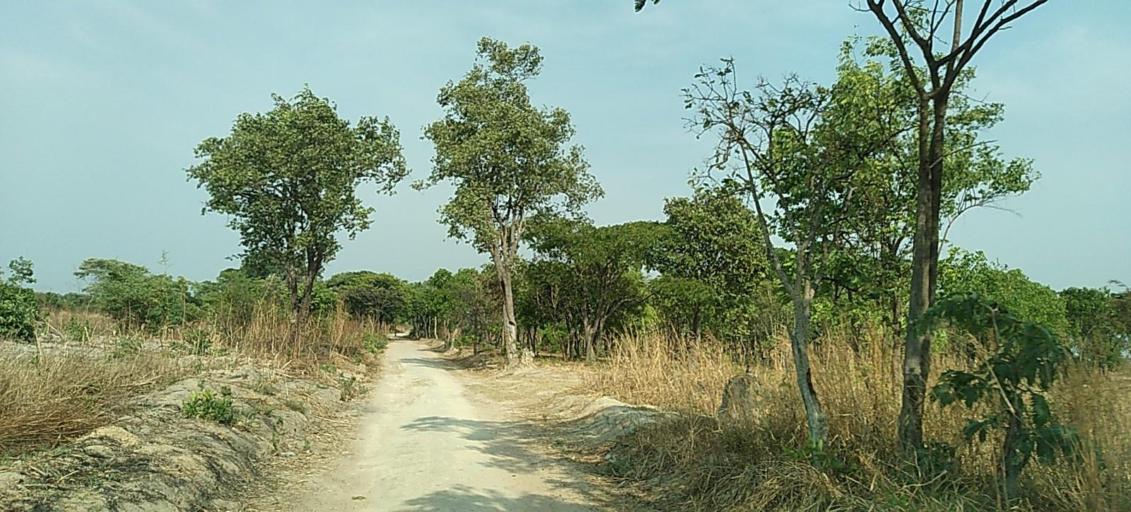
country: ZM
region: Copperbelt
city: Luanshya
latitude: -13.2181
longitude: 28.6541
